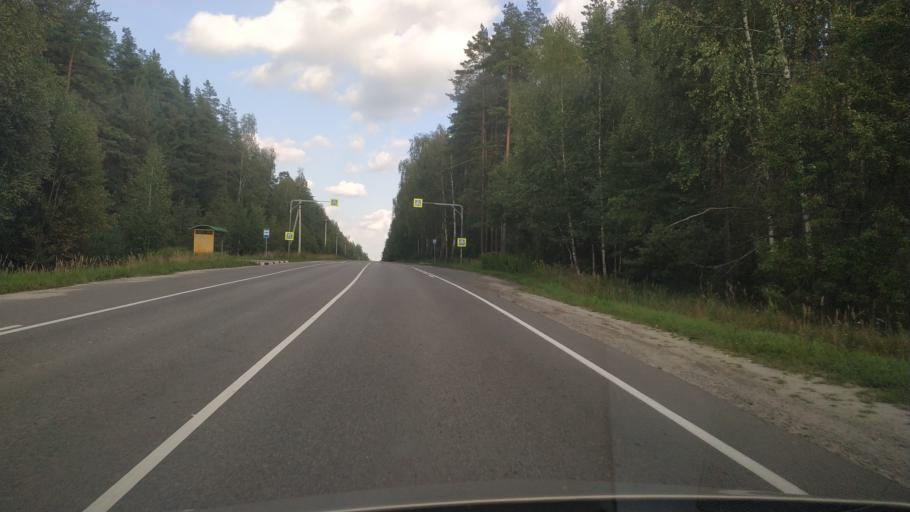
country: RU
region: Moskovskaya
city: Vereya
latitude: 55.7033
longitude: 39.1670
